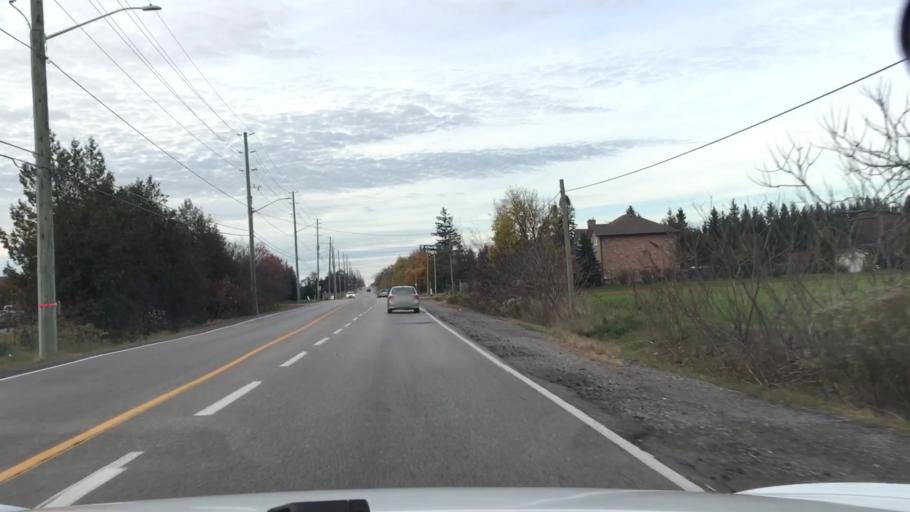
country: CA
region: Ontario
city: Oshawa
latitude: 43.9293
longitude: -78.8233
